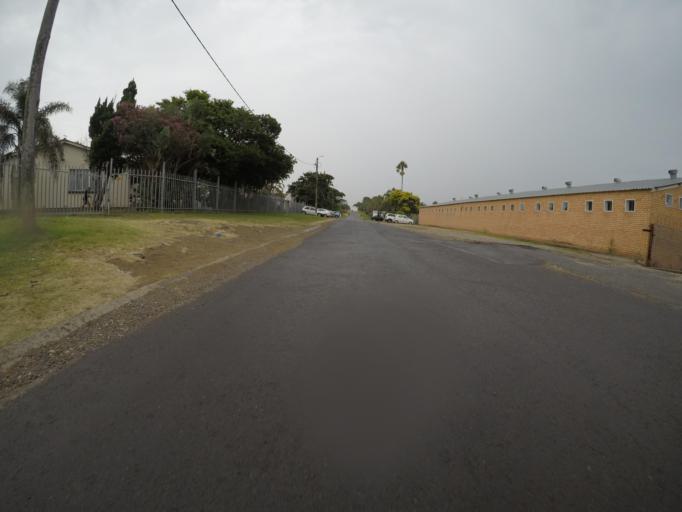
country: ZA
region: Eastern Cape
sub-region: Buffalo City Metropolitan Municipality
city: East London
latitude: -32.9873
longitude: 27.8575
